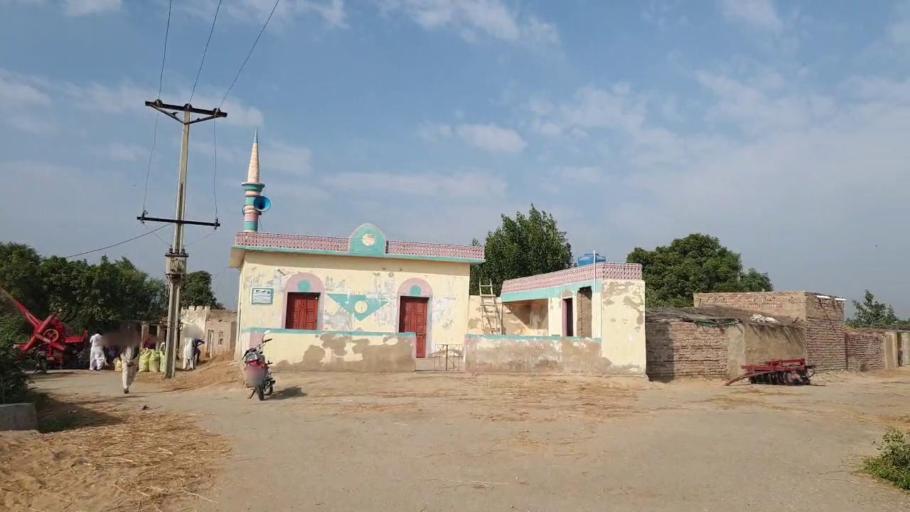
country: PK
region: Sindh
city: Tando Muhammad Khan
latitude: 25.0515
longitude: 68.4338
